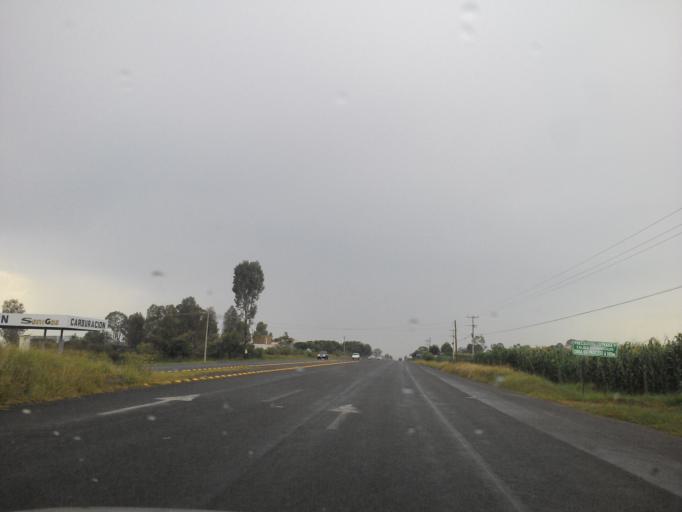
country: MX
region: Jalisco
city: Capilla de Guadalupe
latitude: 20.8698
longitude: -102.6639
